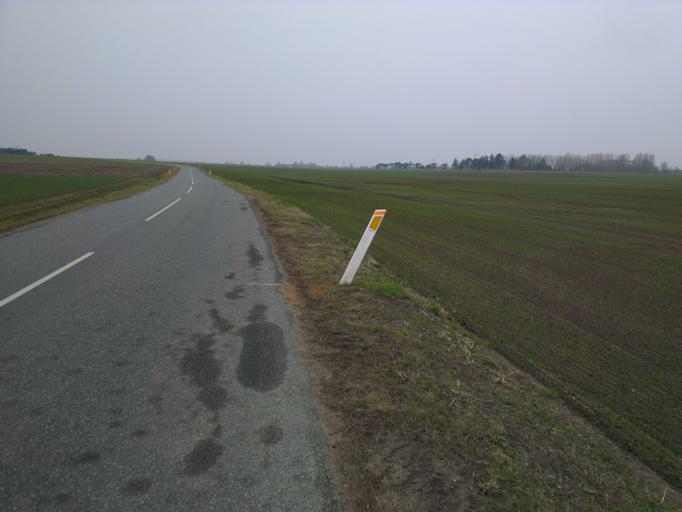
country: DK
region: Capital Region
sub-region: Frederikssund Kommune
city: Skibby
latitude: 55.7875
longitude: 11.9989
